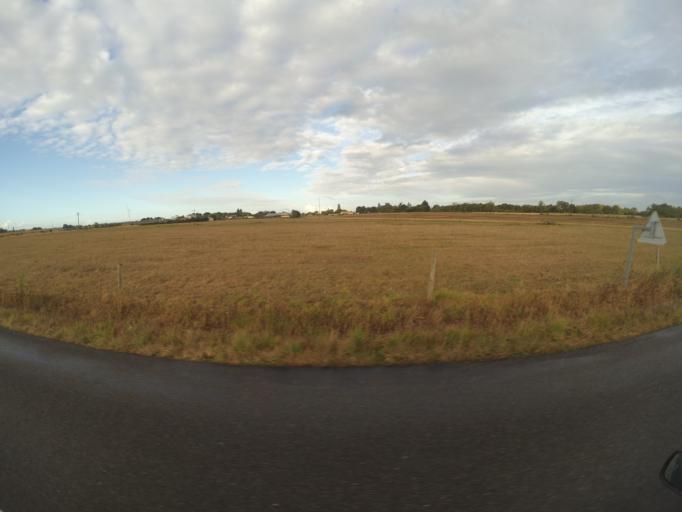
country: FR
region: Pays de la Loire
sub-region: Departement de la Loire-Atlantique
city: La Planche
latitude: 47.0130
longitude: -1.4560
